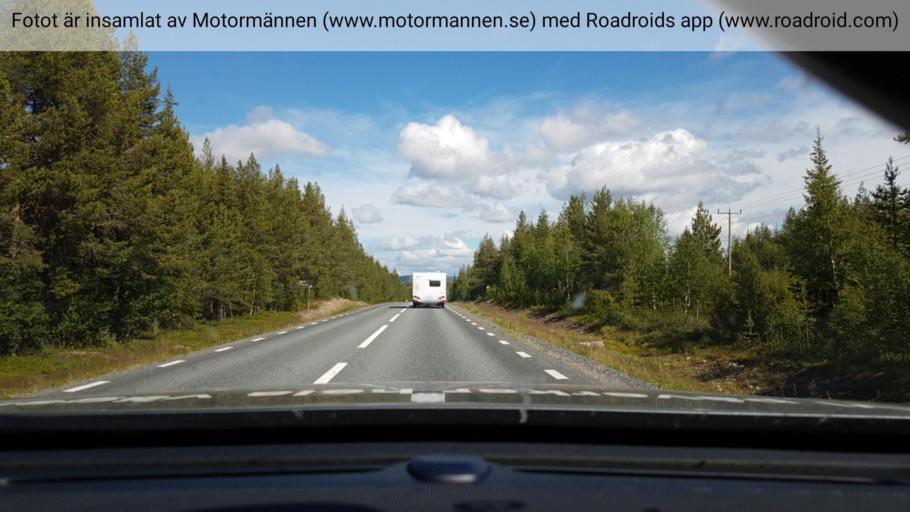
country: SE
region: Norrbotten
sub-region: Arjeplogs Kommun
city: Arjeplog
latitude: 65.5848
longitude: 18.1387
